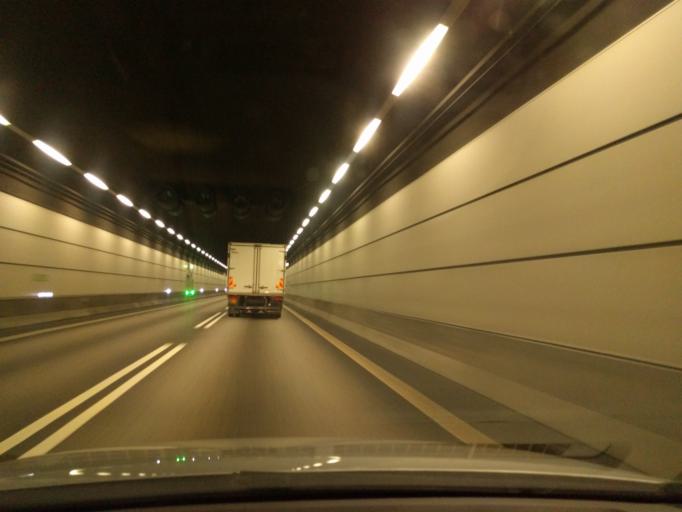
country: DK
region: Capital Region
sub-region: Dragor Kommune
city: Dragor
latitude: 55.6209
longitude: 12.7022
